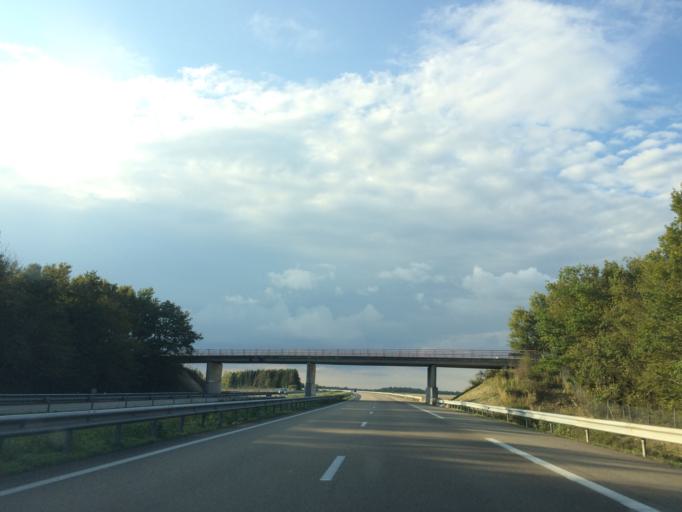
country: FR
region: Bourgogne
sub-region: Departement de l'Yonne
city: Cheroy
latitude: 48.1255
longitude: 2.9676
